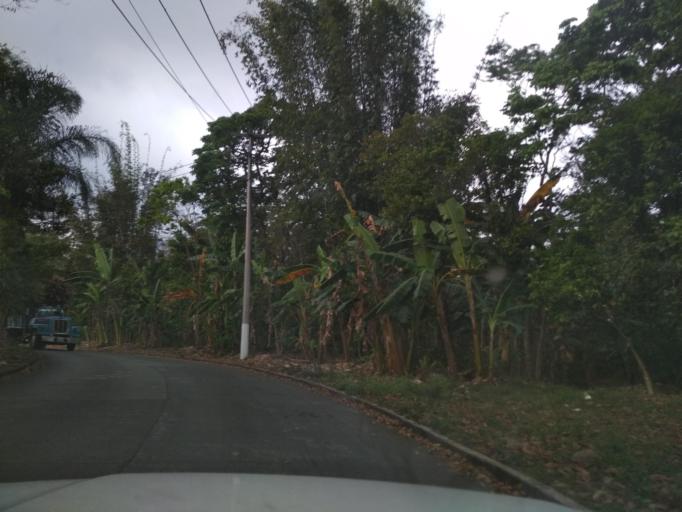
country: MX
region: Veracruz
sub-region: Cordoba
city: San Jose de Tapia
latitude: 18.8397
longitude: -96.9844
